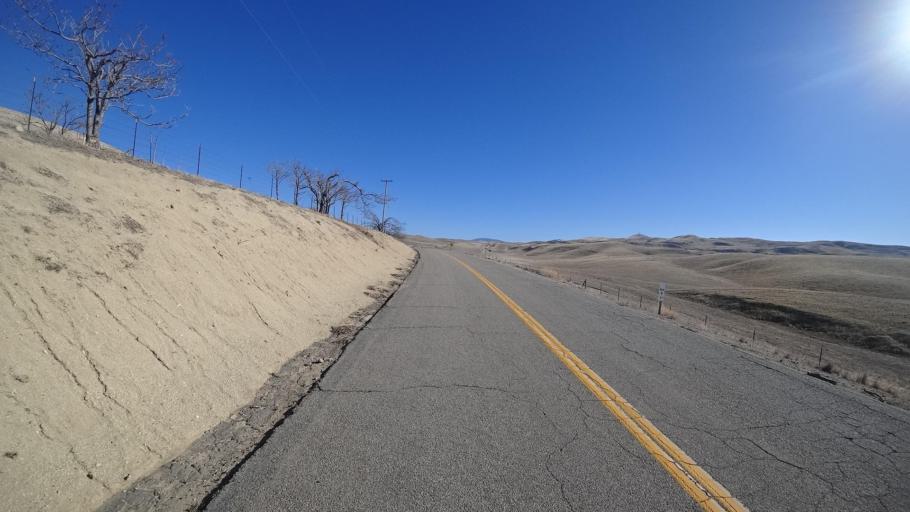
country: US
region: California
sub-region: Kern County
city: Maricopa
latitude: 34.9541
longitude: -119.4324
